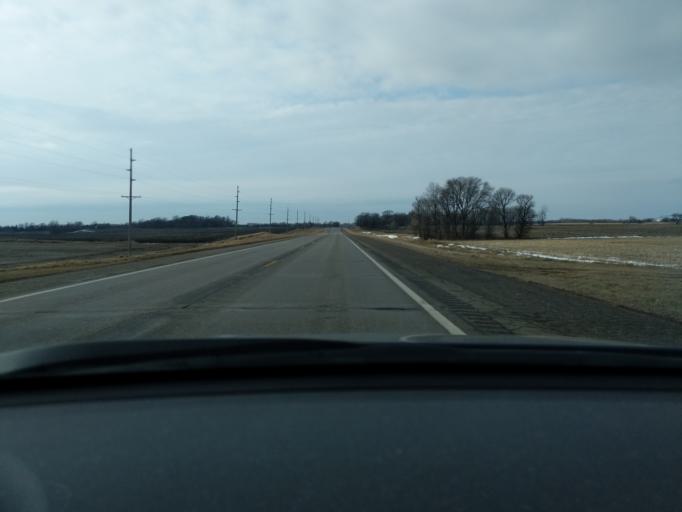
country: US
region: Minnesota
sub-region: Yellow Medicine County
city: Granite Falls
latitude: 44.7889
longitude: -95.4306
